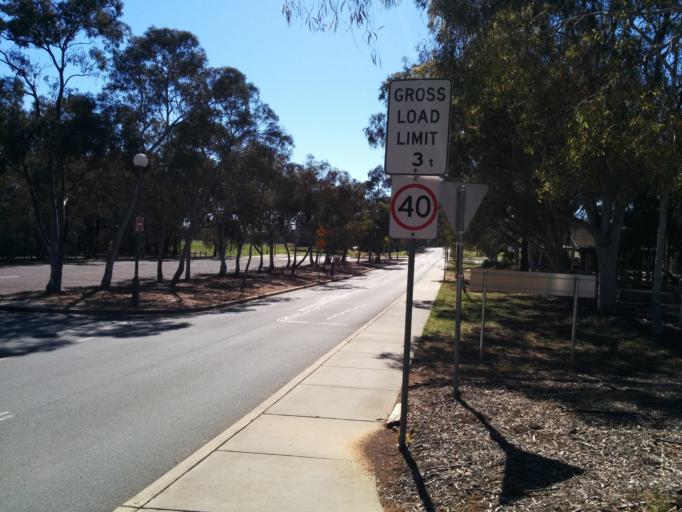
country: AU
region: Australian Capital Territory
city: Belconnen
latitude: -35.2404
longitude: 149.0854
